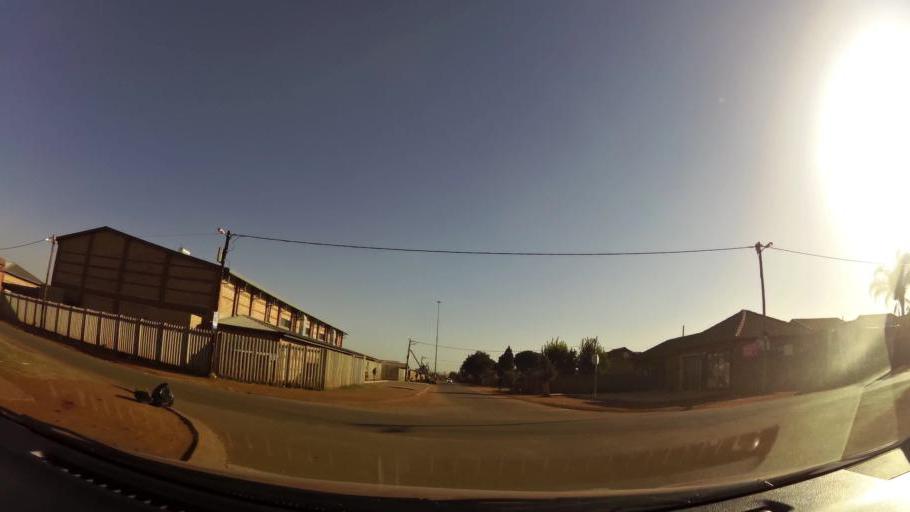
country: ZA
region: Gauteng
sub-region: City of Tshwane Metropolitan Municipality
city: Mabopane
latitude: -25.5878
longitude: 28.0997
